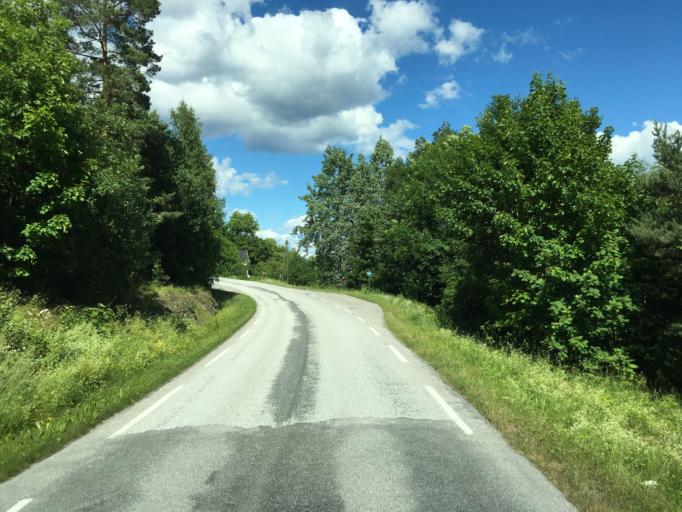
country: NO
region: Oppland
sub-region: Jevnaker
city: Jevnaker
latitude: 60.3391
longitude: 10.3578
